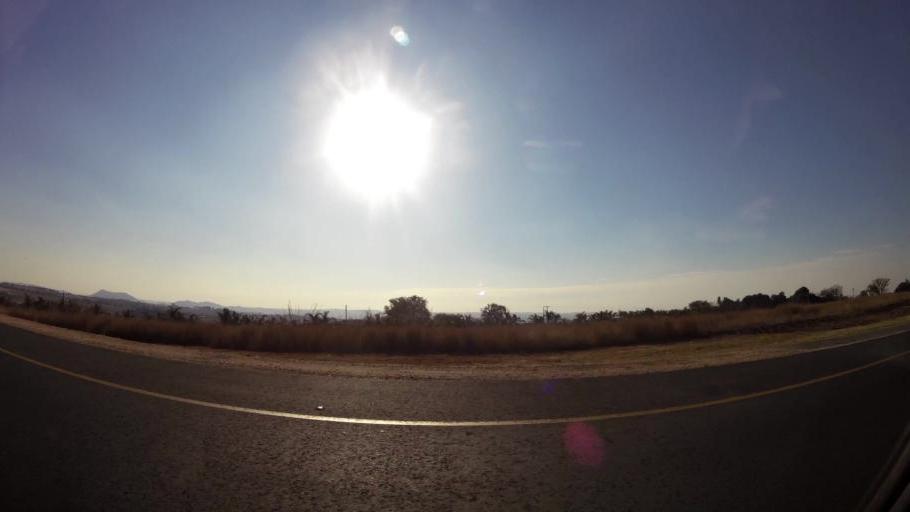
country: ZA
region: Gauteng
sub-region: West Rand District Municipality
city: Muldersdriseloop
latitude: -25.9902
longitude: 27.9156
